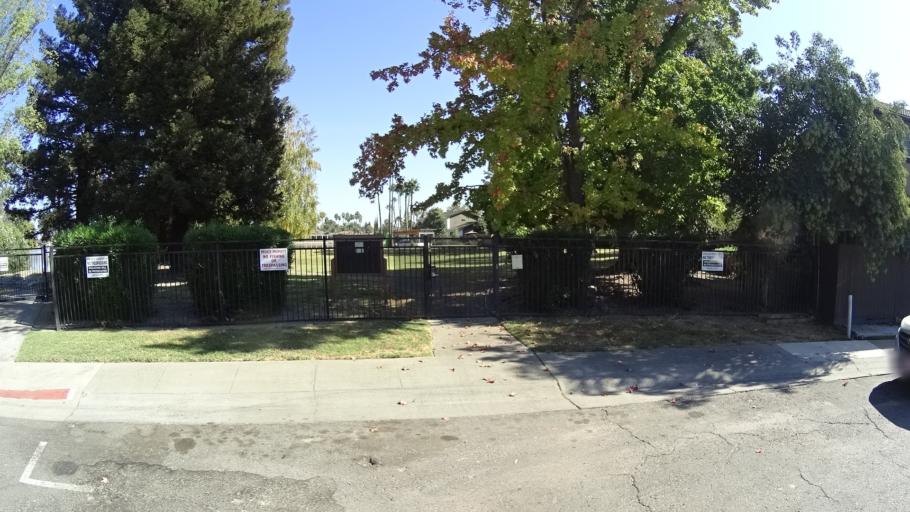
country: US
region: California
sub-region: Yolo County
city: West Sacramento
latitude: 38.5063
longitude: -121.5380
